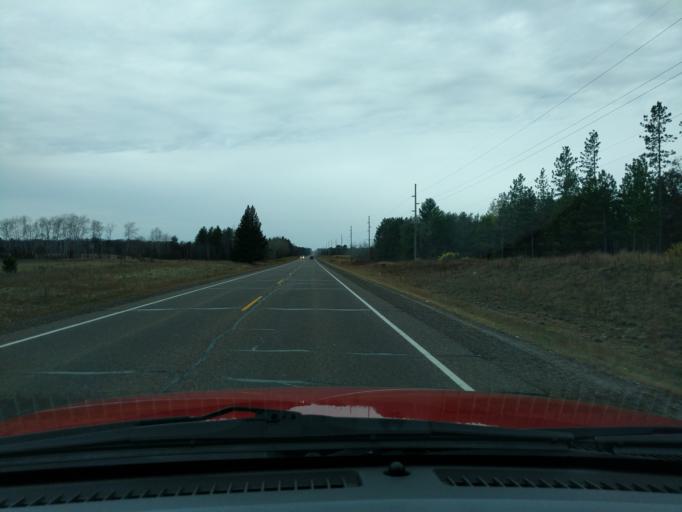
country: US
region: Wisconsin
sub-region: Washburn County
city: Spooner
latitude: 45.8151
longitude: -91.9833
